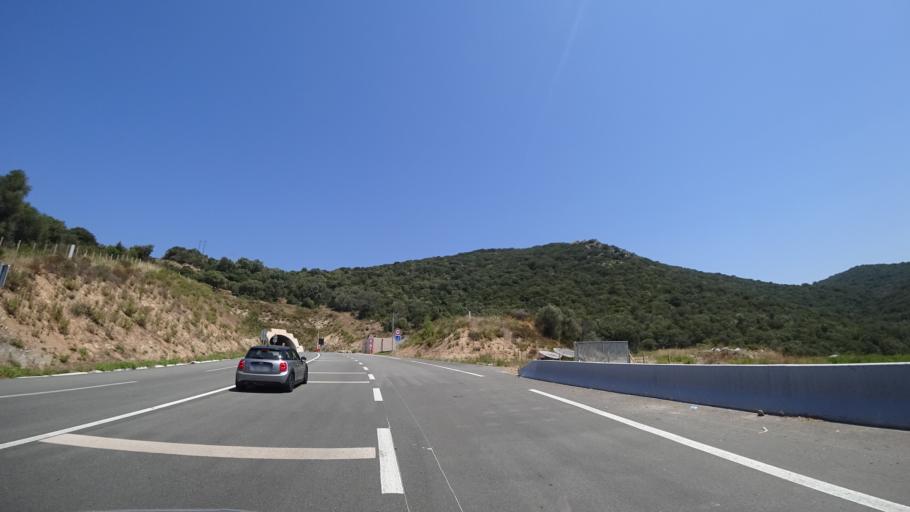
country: FR
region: Corsica
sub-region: Departement de la Corse-du-Sud
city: Propriano
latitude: 41.6689
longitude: 8.9263
